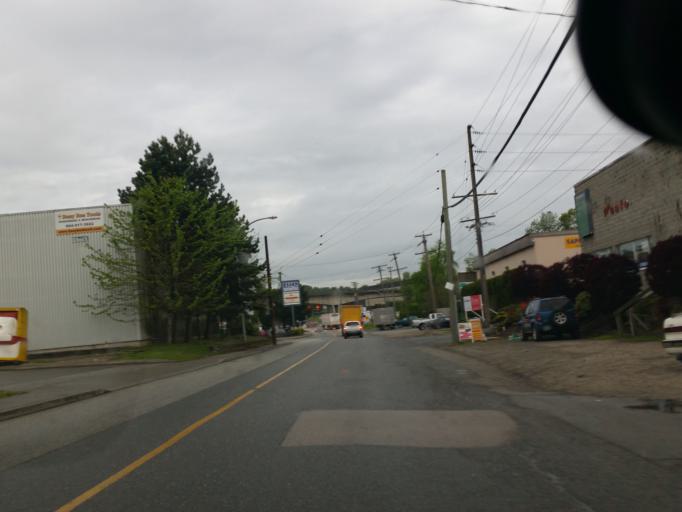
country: CA
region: British Columbia
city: New Westminster
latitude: 49.2299
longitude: -122.8789
